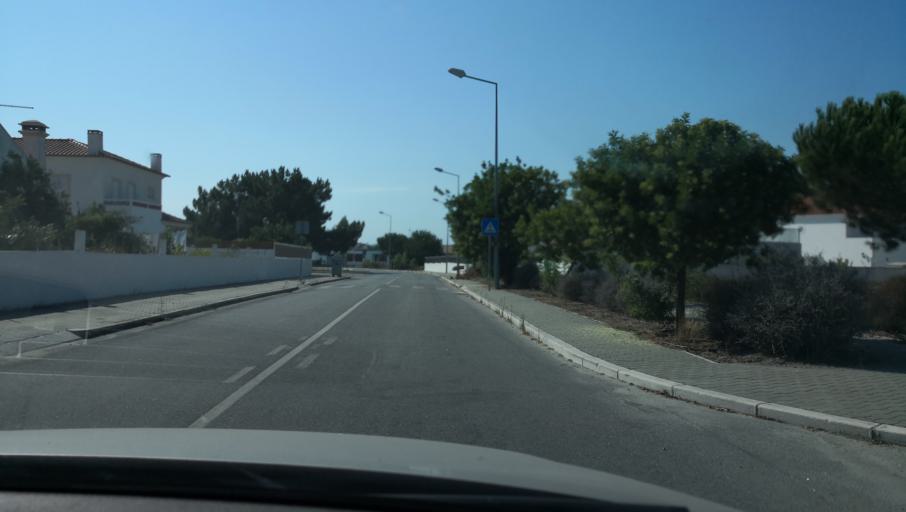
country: PT
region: Setubal
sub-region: Setubal
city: Setubal
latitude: 38.3977
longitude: -8.7708
